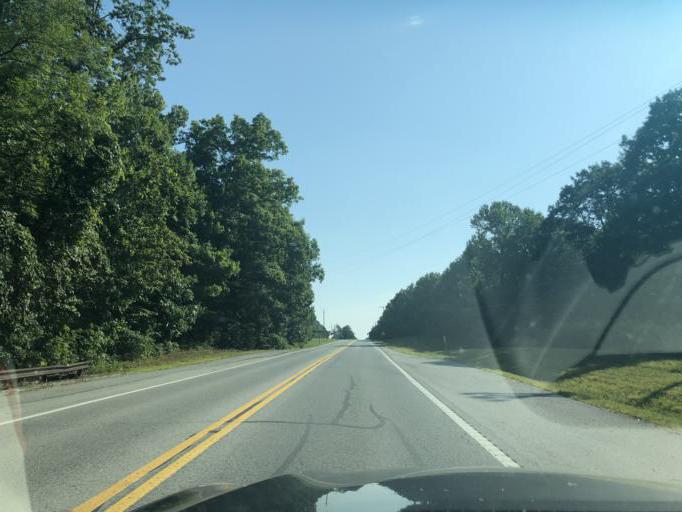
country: US
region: Tennessee
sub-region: Franklin County
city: Sewanee
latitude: 35.2086
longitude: -85.9004
